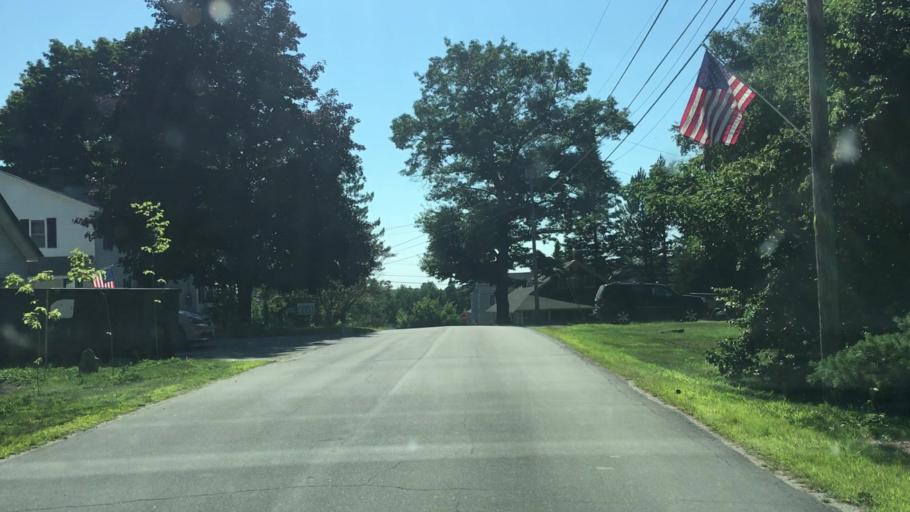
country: US
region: Maine
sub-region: Penobscot County
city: Enfield
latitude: 45.2467
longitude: -68.5648
